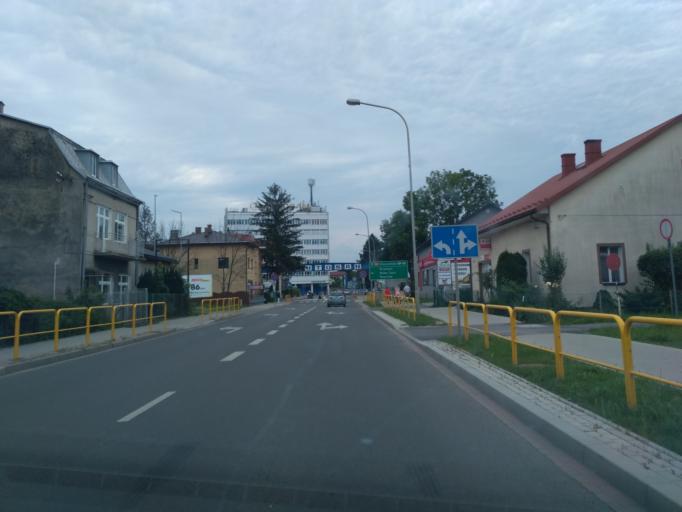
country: PL
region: Subcarpathian Voivodeship
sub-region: Powiat sanocki
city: Sanok
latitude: 49.5486
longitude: 22.2155
